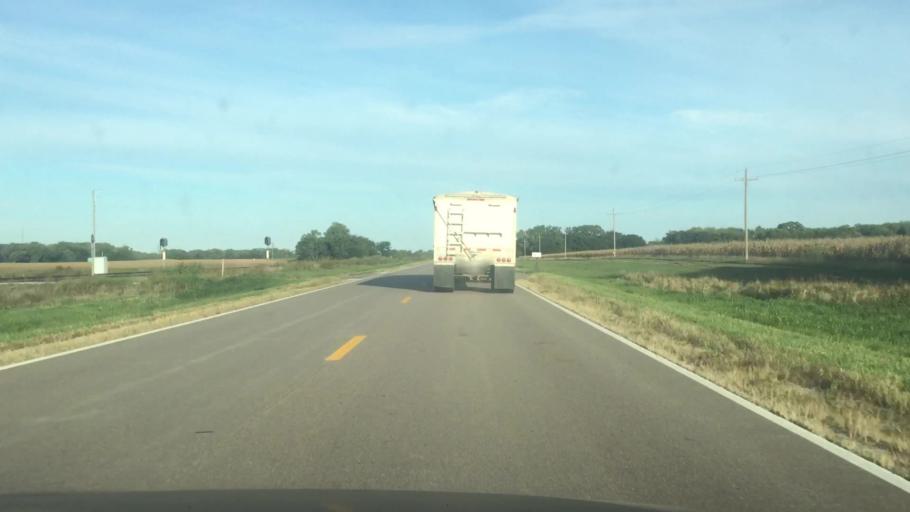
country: US
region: Nebraska
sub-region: Jefferson County
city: Fairbury
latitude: 40.0527
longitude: -97.0337
